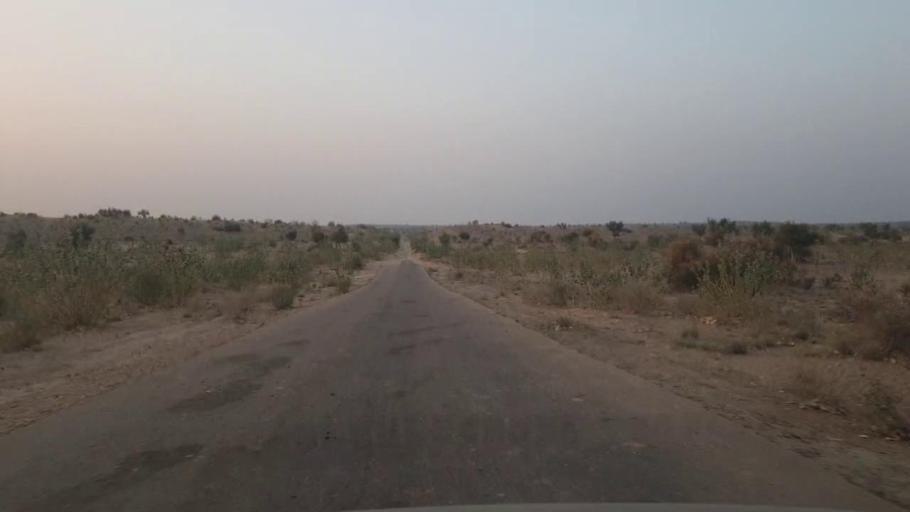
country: PK
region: Sindh
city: Umarkot
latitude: 25.2959
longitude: 70.0756
